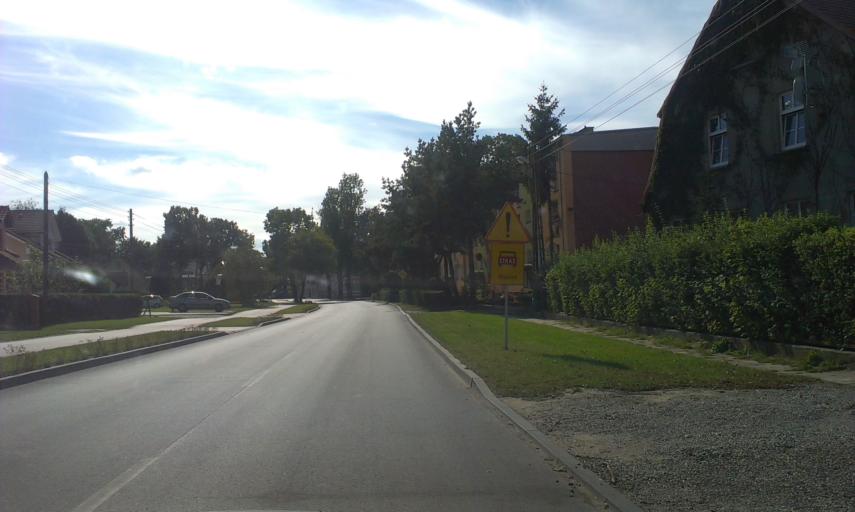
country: PL
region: Greater Poland Voivodeship
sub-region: Powiat pilski
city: Lobzenica
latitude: 53.2643
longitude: 17.2567
